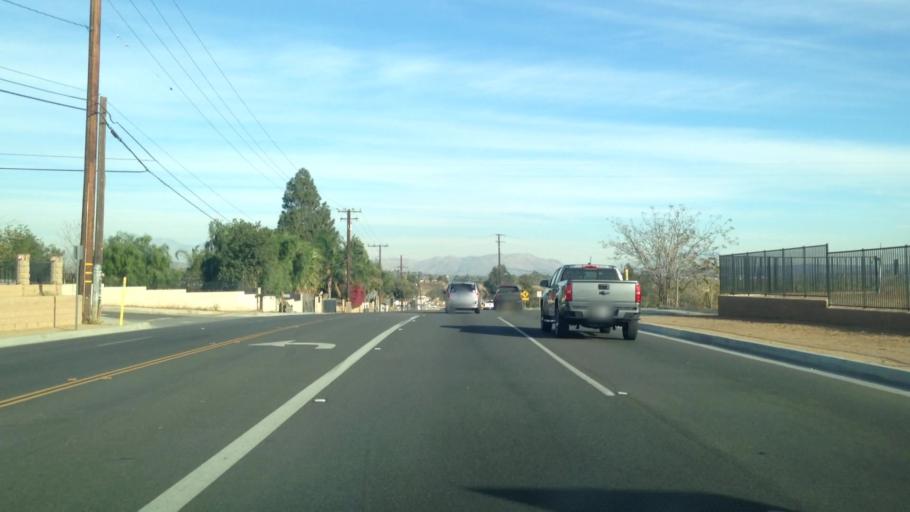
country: US
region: California
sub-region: Riverside County
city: Mira Loma
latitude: 33.9755
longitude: -117.5195
